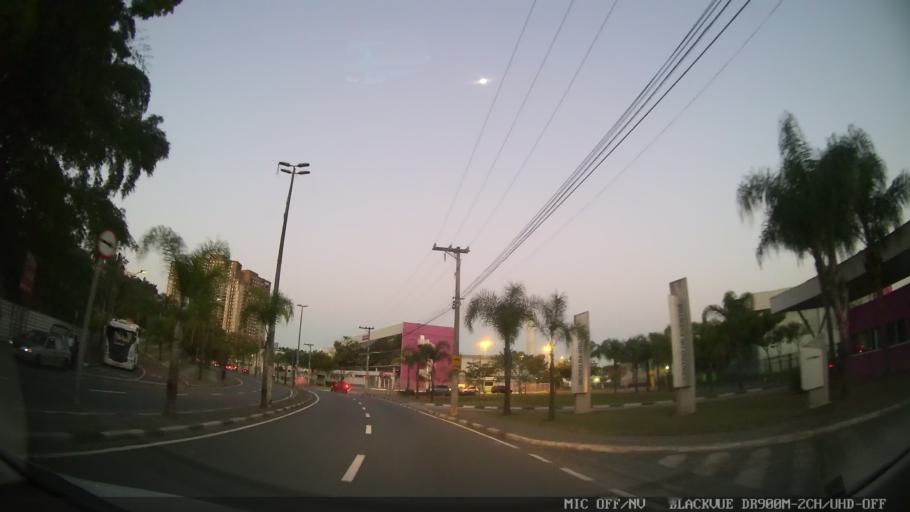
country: BR
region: Sao Paulo
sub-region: Barueri
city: Barueri
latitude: -23.4966
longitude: -46.8709
